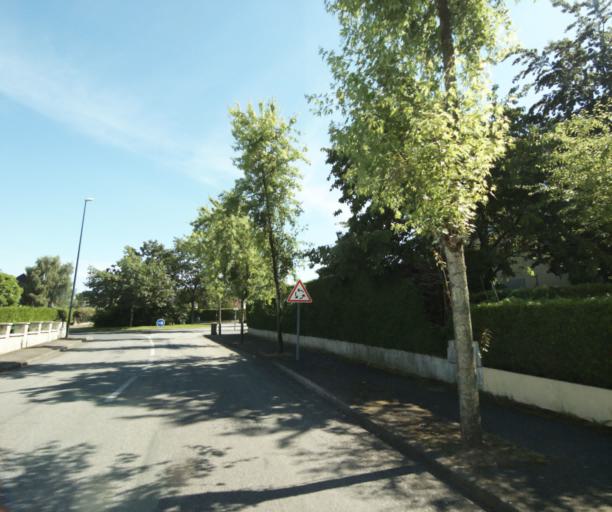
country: FR
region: Pays de la Loire
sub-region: Departement de la Mayenne
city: Laval
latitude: 48.0611
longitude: -0.7991
